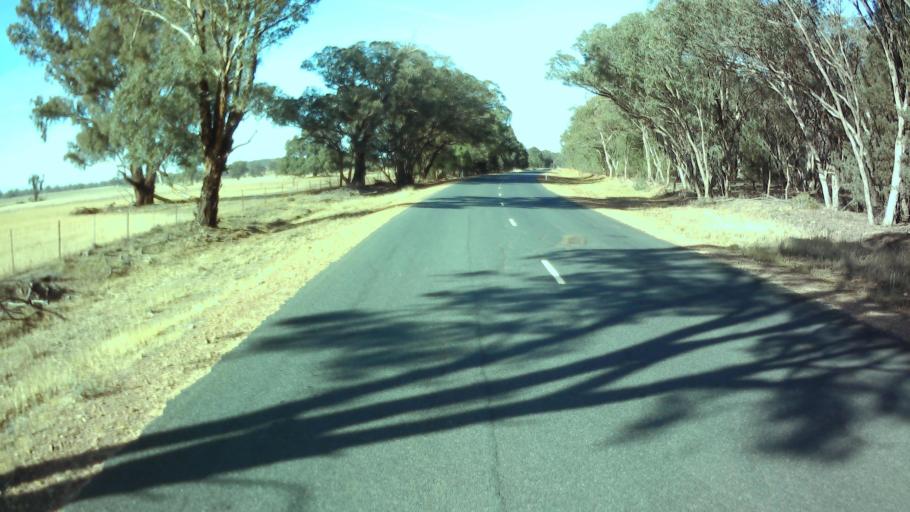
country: AU
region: New South Wales
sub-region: Weddin
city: Grenfell
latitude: -34.0172
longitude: 148.1081
